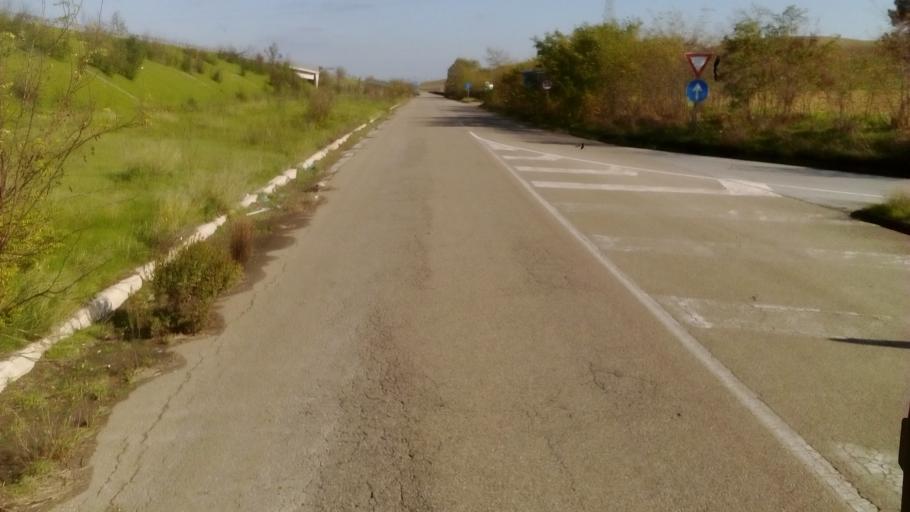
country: IT
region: Basilicate
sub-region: Provincia di Potenza
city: Melfi
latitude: 41.0651
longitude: 15.6807
